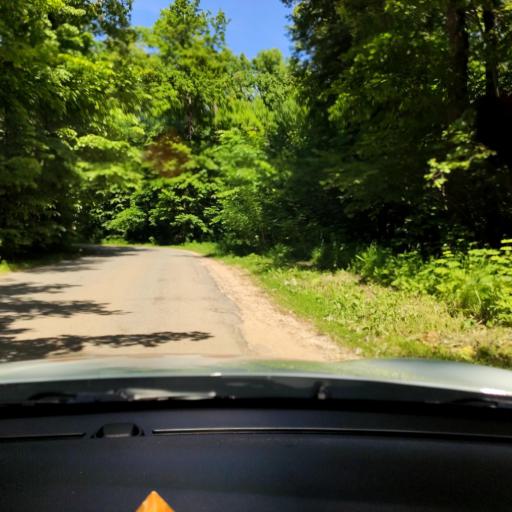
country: RU
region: Tatarstan
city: Osinovo
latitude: 55.7783
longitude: 48.7962
